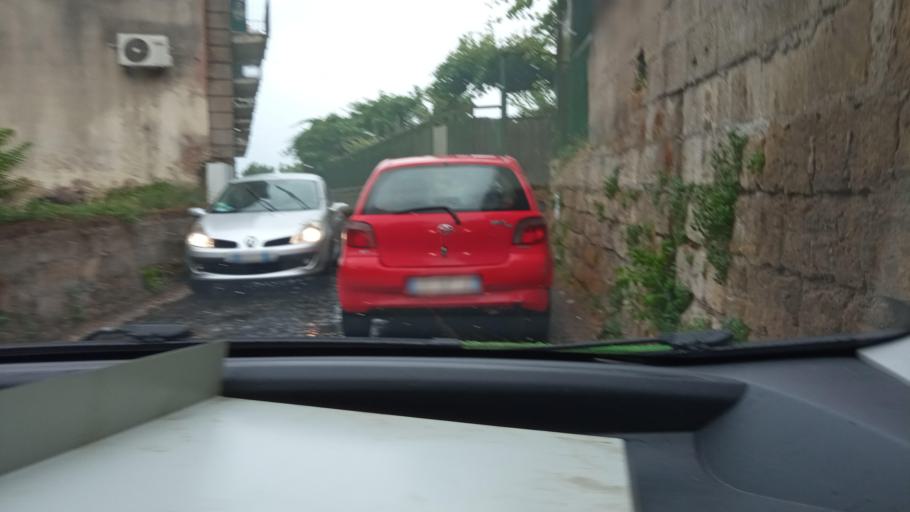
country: IT
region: Campania
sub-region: Provincia di Napoli
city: Quarto
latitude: 40.8430
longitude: 14.1179
